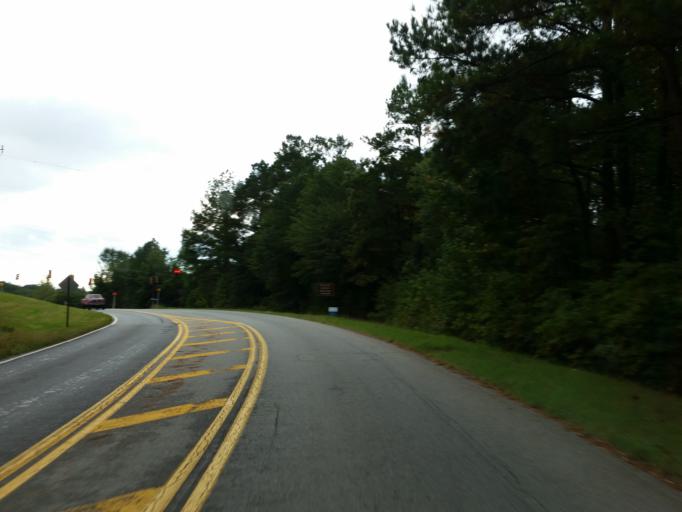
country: US
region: Georgia
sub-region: Bartow County
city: Cartersville
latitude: 34.1172
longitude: -84.8193
